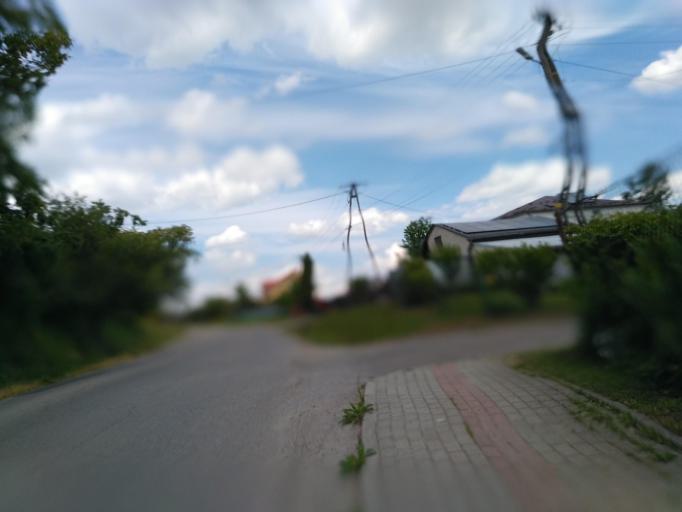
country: PL
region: Subcarpathian Voivodeship
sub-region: Powiat krosnienski
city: Chorkowka
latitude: 49.6122
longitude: 21.6457
